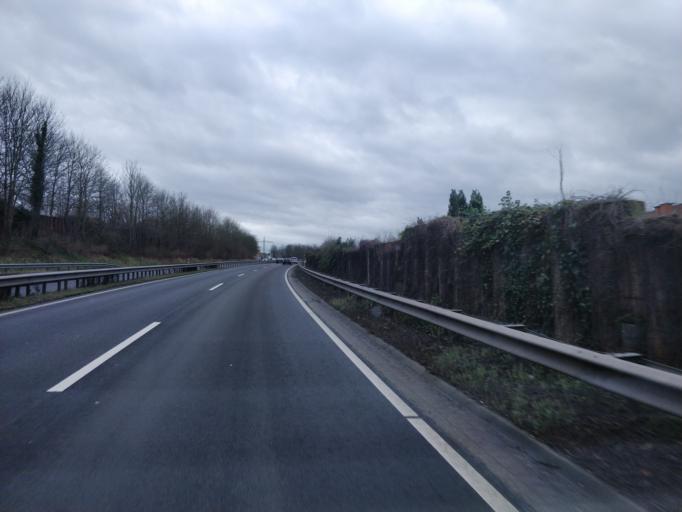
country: DE
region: Rheinland-Pfalz
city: Melsbach
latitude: 50.4641
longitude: 7.4860
